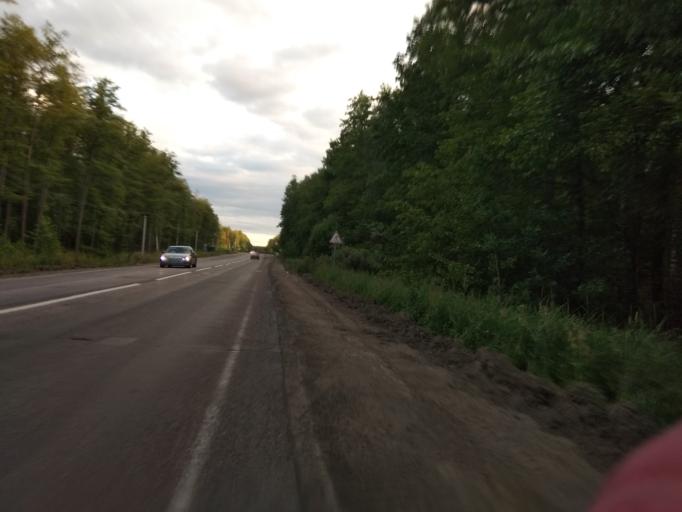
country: RU
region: Moskovskaya
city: Misheronskiy
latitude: 55.6360
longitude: 39.7483
